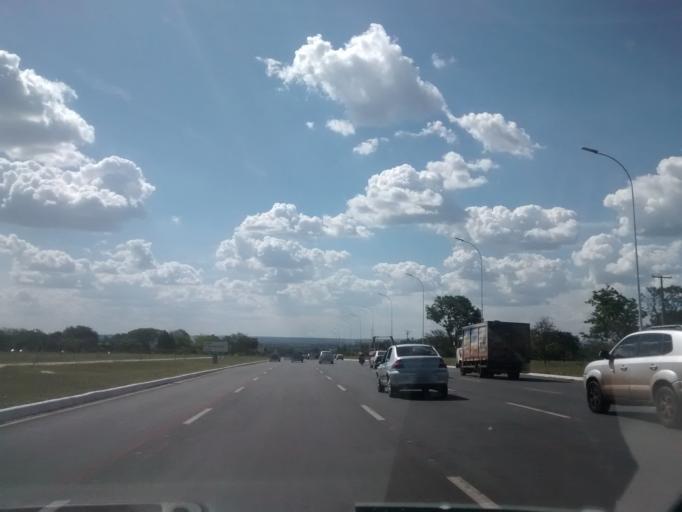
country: BR
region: Federal District
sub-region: Brasilia
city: Brasilia
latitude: -15.7822
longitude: -47.9170
